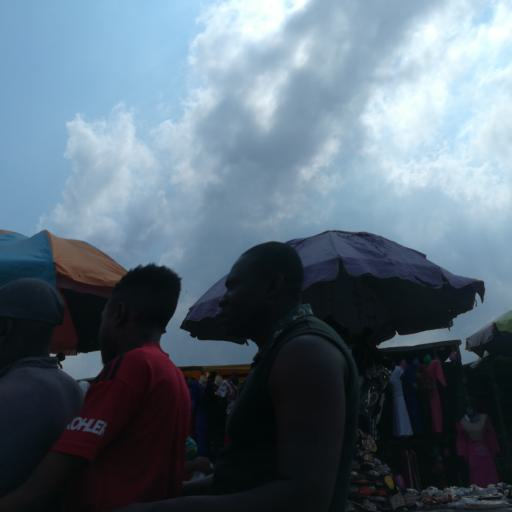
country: NG
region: Rivers
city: Okrika
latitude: 4.7902
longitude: 7.1194
